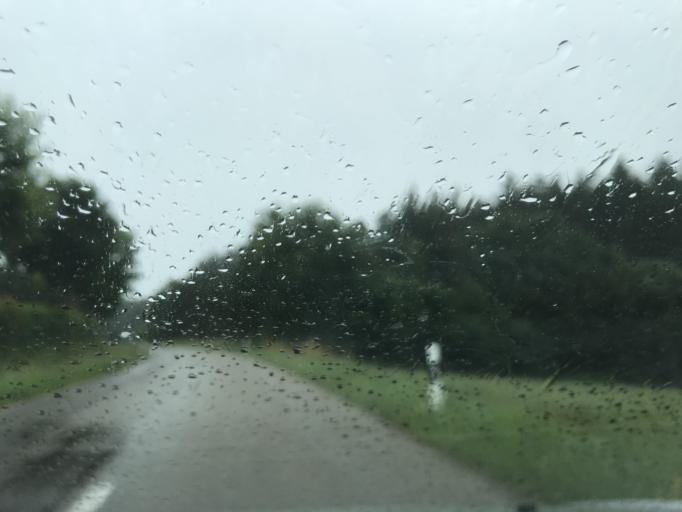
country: DE
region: Bavaria
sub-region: Upper Bavaria
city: Jetzendorf
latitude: 48.4441
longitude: 11.4551
